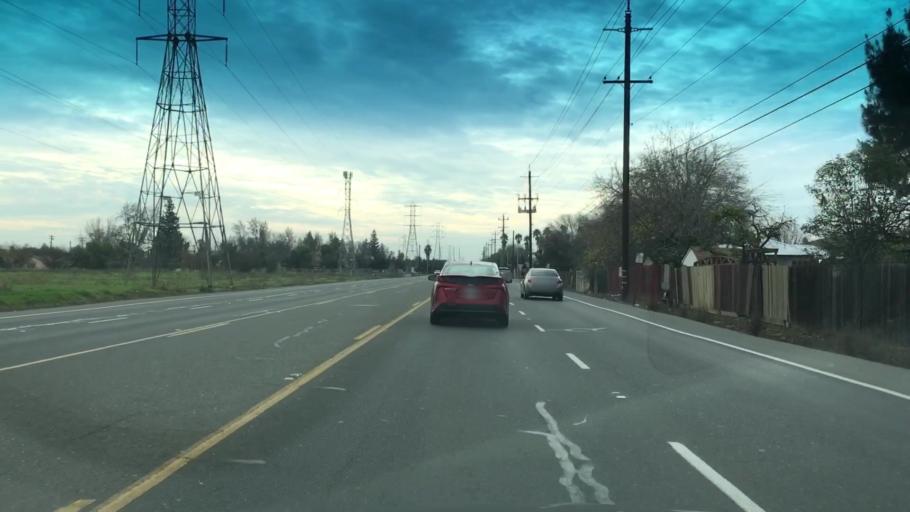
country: US
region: California
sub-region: Sacramento County
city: Florin
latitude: 38.4942
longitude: -121.4090
